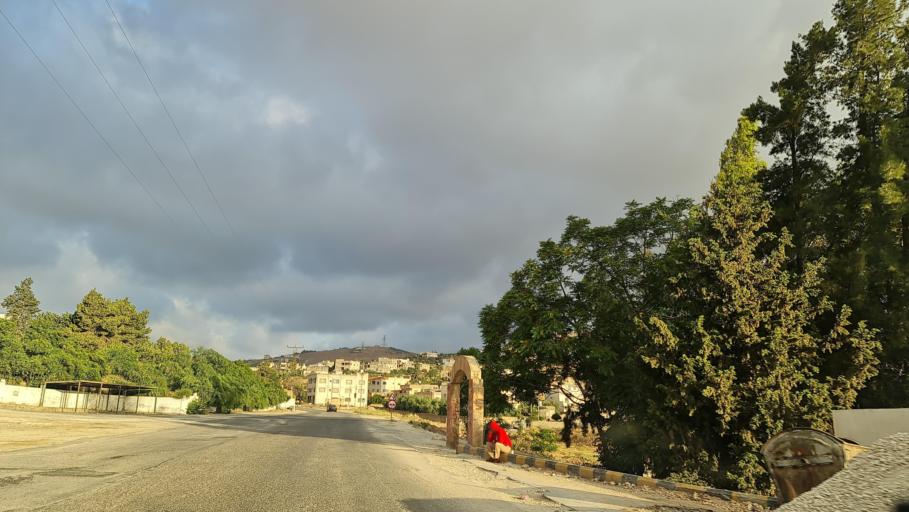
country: JO
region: Amman
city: Al Jubayhah
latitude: 32.0926
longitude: 35.9276
